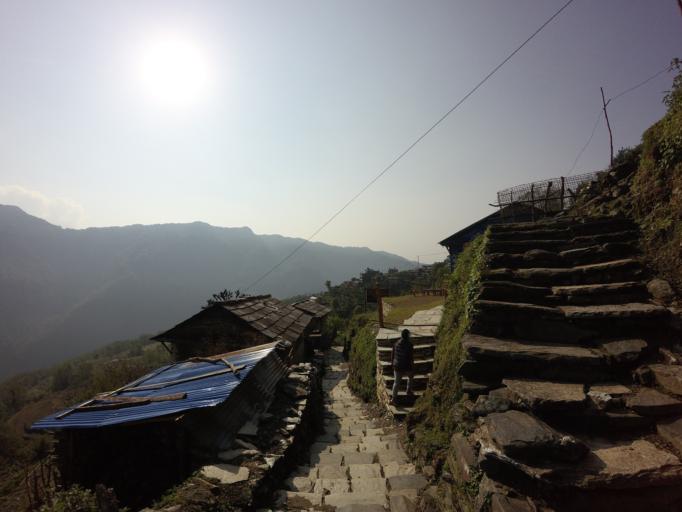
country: NP
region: Western Region
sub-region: Dhawalagiri Zone
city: Chitre
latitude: 28.3798
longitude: 83.8065
